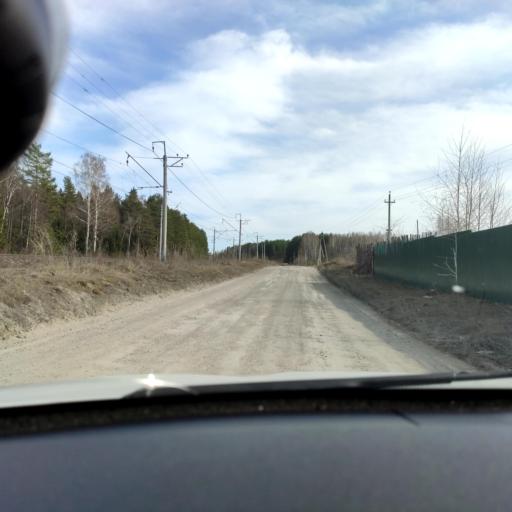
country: RU
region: Perm
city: Overyata
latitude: 58.0585
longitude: 55.9908
